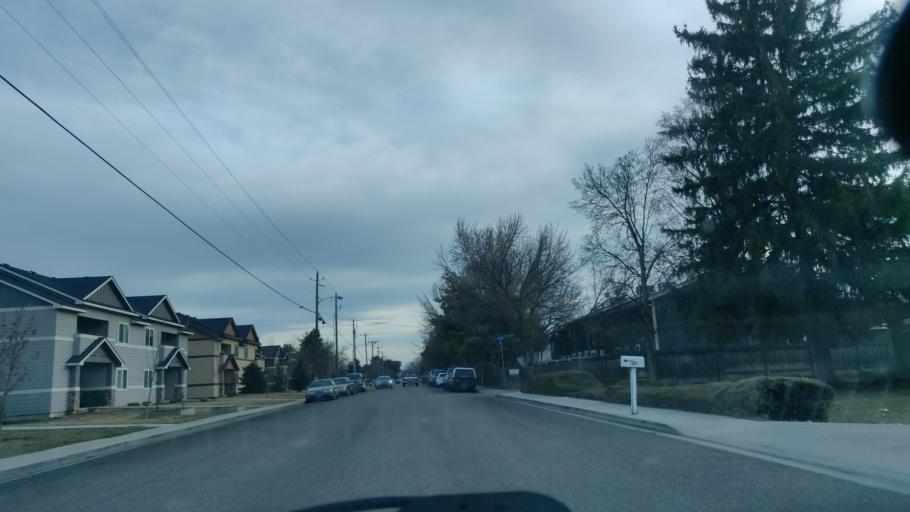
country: US
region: Idaho
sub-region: Ada County
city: Garden City
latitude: 43.6170
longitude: -116.2662
